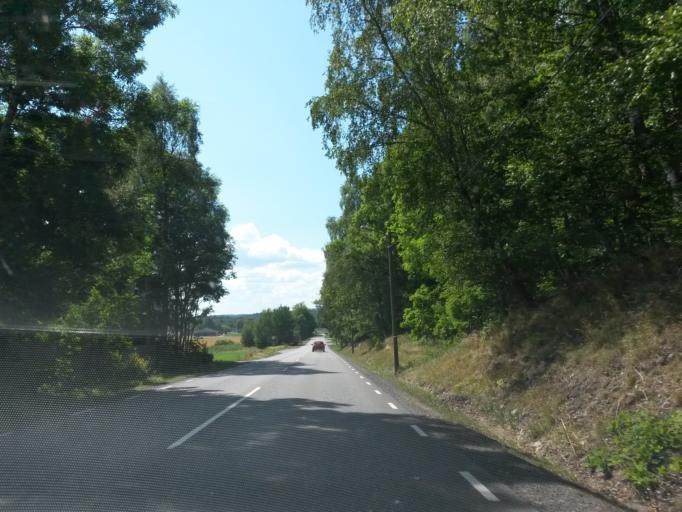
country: SE
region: Vaestra Goetaland
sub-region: Lerums Kommun
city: Grabo
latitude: 57.9224
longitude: 12.3554
